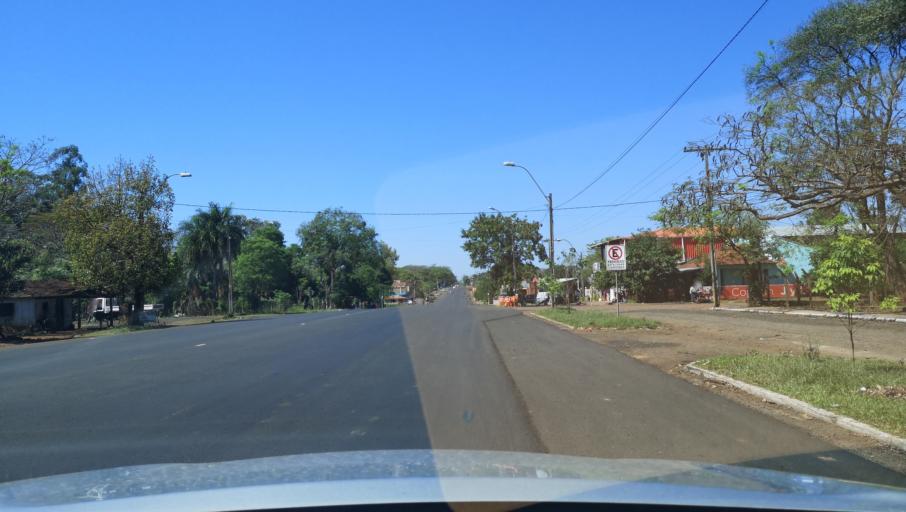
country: PY
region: Itapua
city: Carmen del Parana
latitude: -27.1566
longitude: -56.2295
